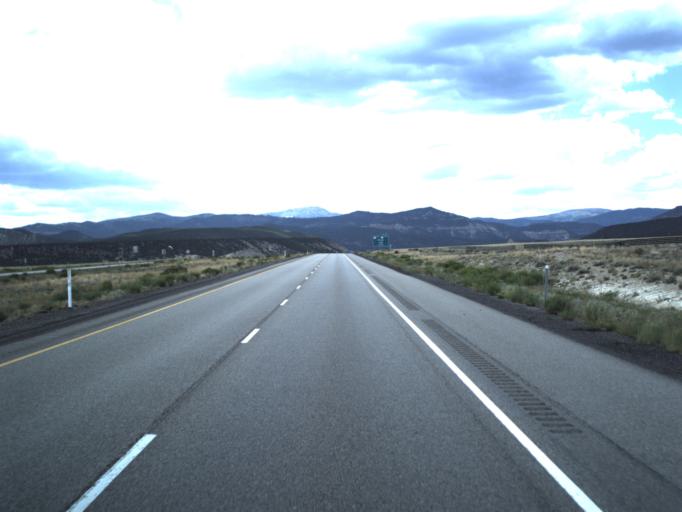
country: US
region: Utah
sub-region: Emery County
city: Ferron
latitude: 38.7724
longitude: -111.3317
